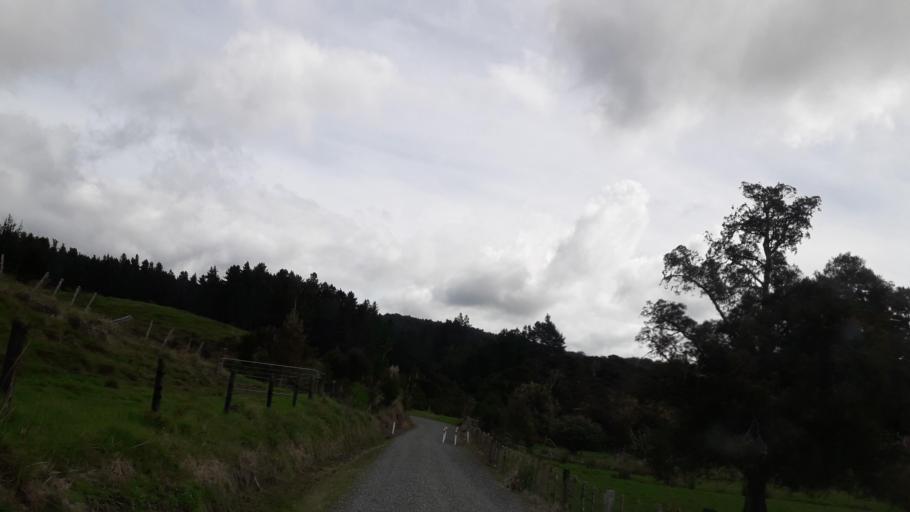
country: NZ
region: Northland
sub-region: Far North District
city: Waimate North
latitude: -35.1561
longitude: 173.7134
